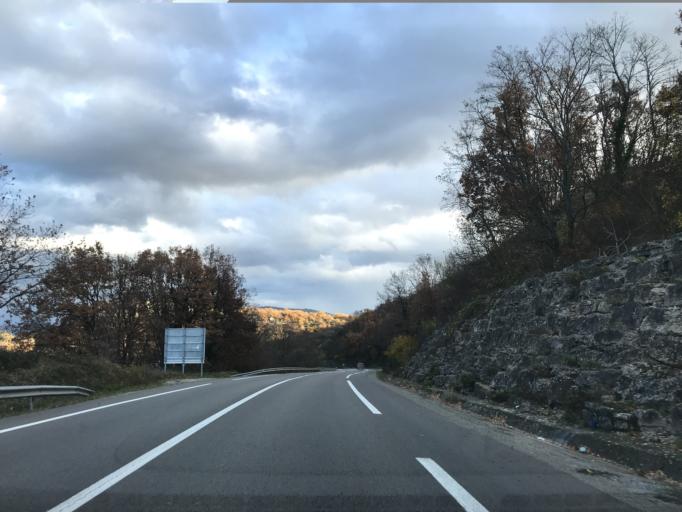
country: FR
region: Rhone-Alpes
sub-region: Departement de l'Ardeche
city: Alissas
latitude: 44.7127
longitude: 4.6179
